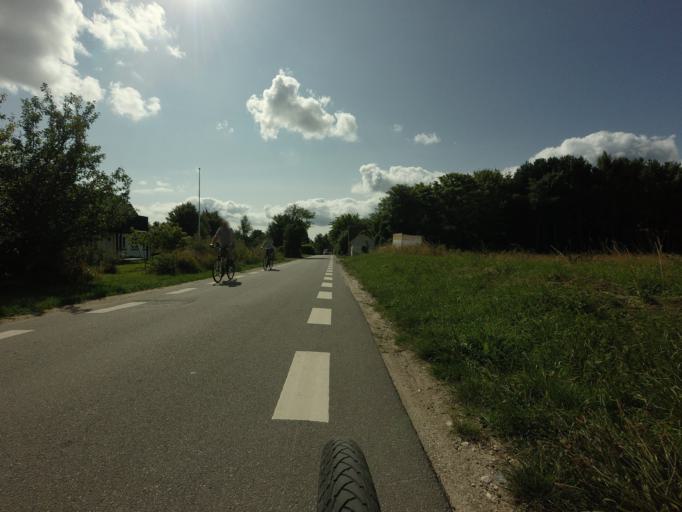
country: DK
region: Zealand
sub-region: Vordingborg Kommune
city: Stege
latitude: 54.9702
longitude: 12.3869
